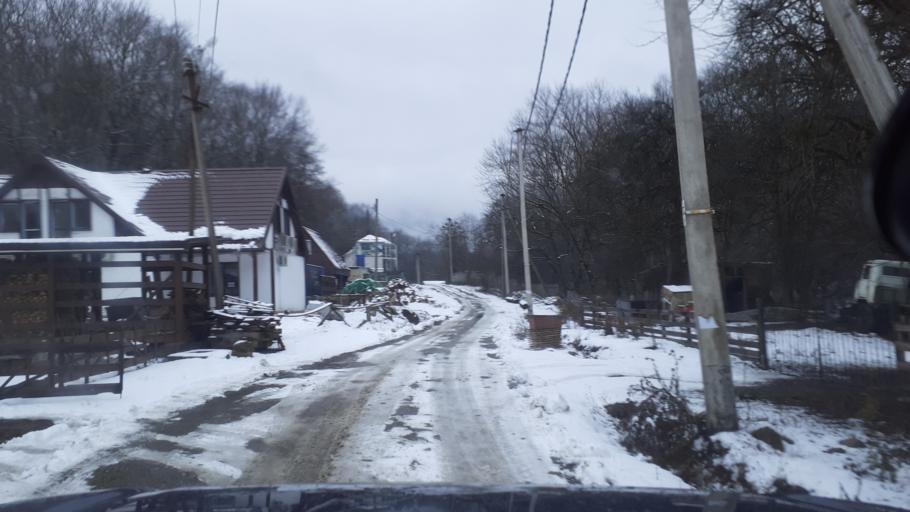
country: RU
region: Adygeya
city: Kamennomostskiy
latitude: 44.1122
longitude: 40.1172
